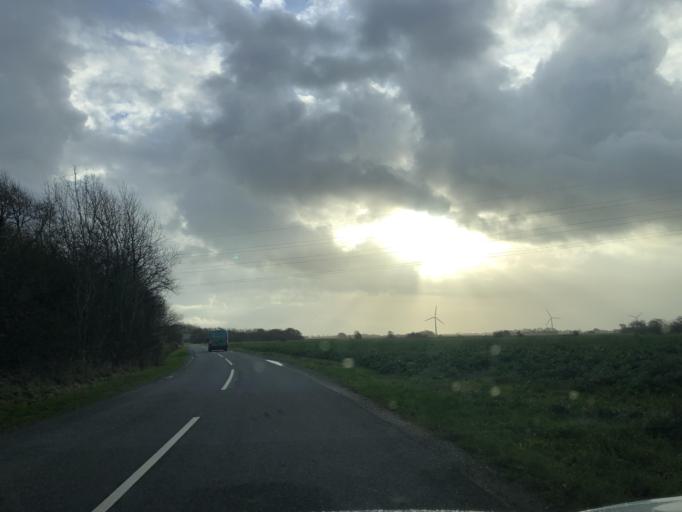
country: DK
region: South Denmark
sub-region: Esbjerg Kommune
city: Bramming
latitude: 55.4171
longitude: 8.7066
